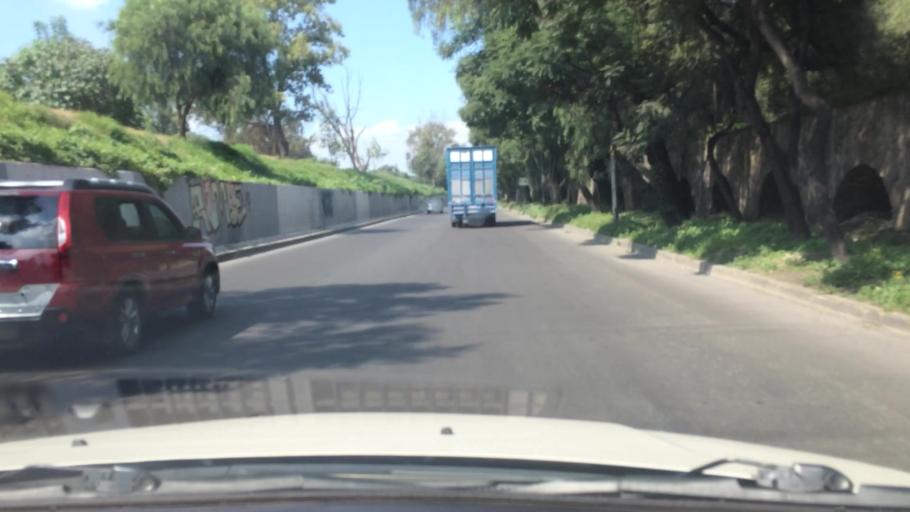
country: MX
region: Mexico
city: Colonia Lindavista
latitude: 19.5210
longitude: -99.1477
